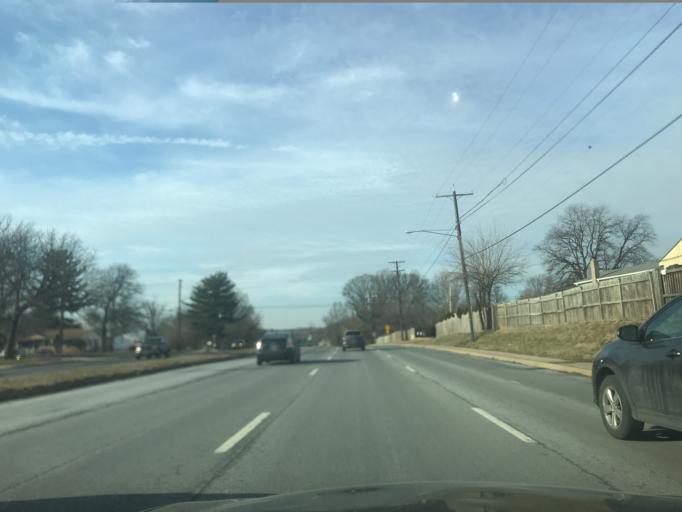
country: US
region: Maryland
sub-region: Montgomery County
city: Aspen Hill
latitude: 39.0701
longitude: -77.0625
